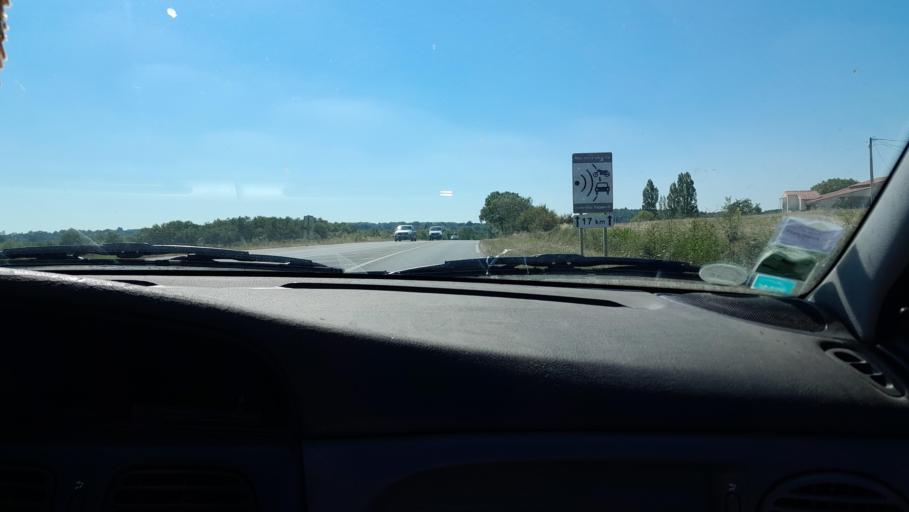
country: FR
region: Pays de la Loire
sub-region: Departement de la Loire-Atlantique
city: Saint-Gereon
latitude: 47.3677
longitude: -1.2172
